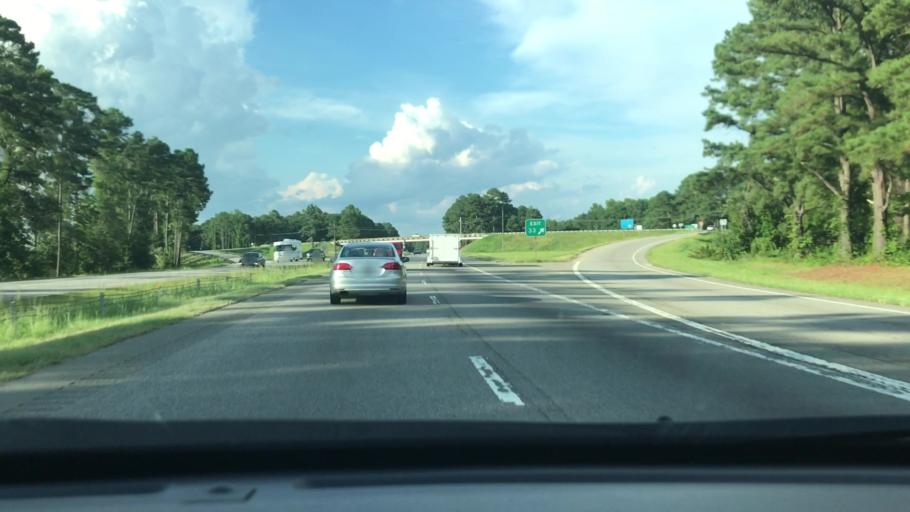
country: US
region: North Carolina
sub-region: Robeson County
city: Saint Pauls
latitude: 34.8311
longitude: -78.9806
